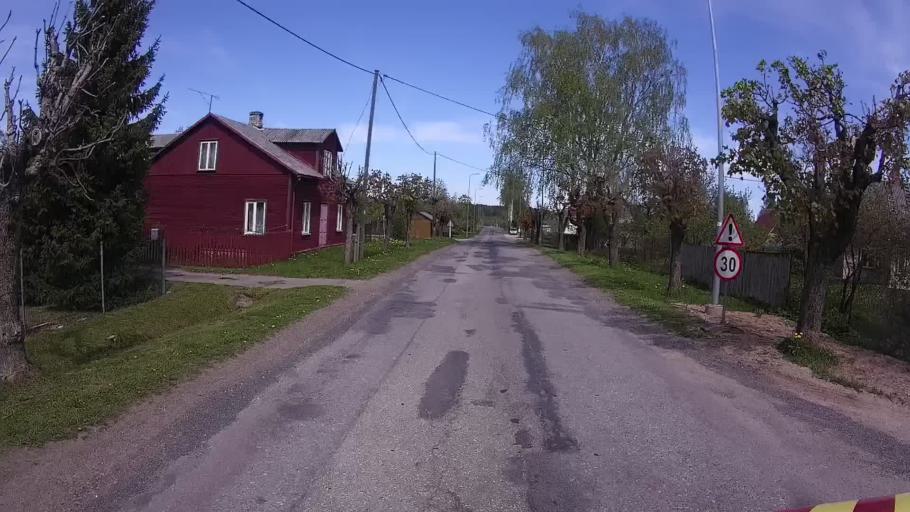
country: EE
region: Valgamaa
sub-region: Valga linn
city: Valga
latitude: 57.7714
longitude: 26.0677
